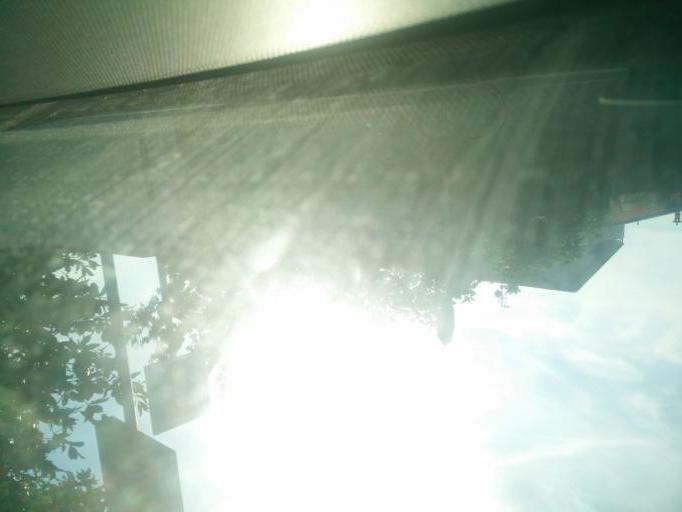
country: IT
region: Tuscany
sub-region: Provincia di Massa-Carrara
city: Massa
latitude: 44.0237
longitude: 10.1228
